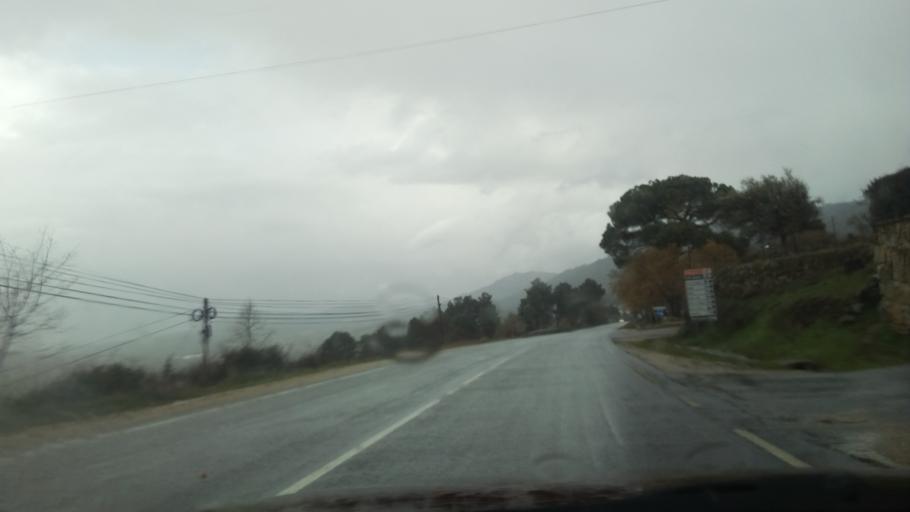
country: PT
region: Guarda
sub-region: Guarda
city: Guarda
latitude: 40.5800
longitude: -7.2947
